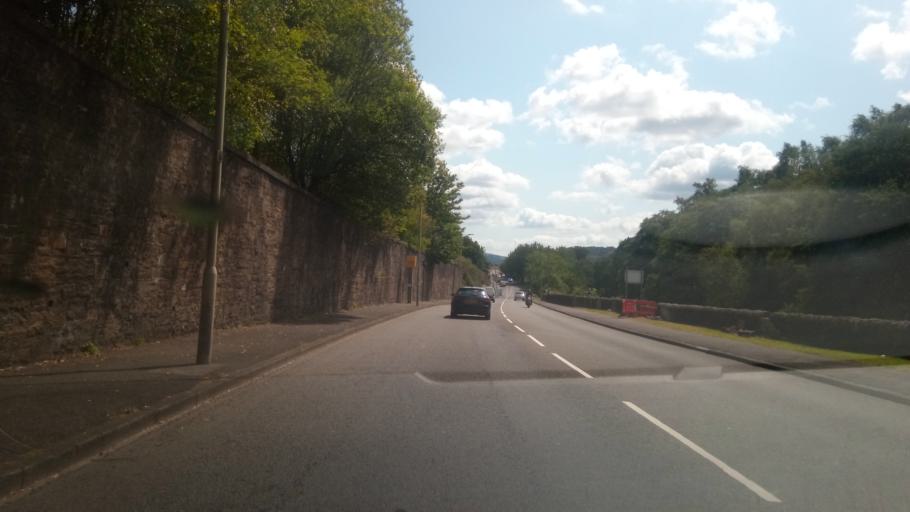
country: GB
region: Wales
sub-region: Rhondda Cynon Taf
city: Pontypridd
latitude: 51.6086
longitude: -3.3652
